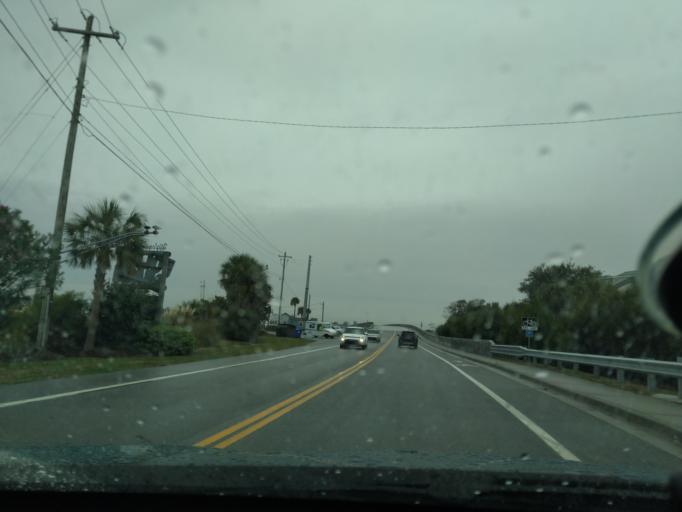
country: US
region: South Carolina
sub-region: Charleston County
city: Folly Beach
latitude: 32.6736
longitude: -79.9491
